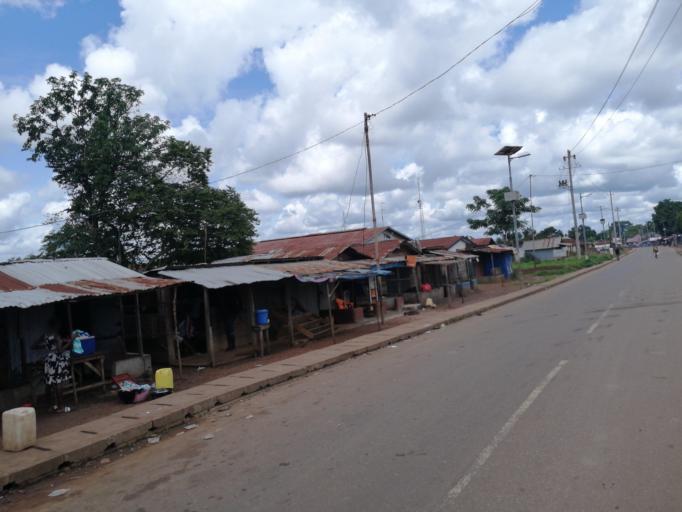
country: SL
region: Northern Province
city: Port Loko
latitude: 8.7742
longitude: -12.7875
